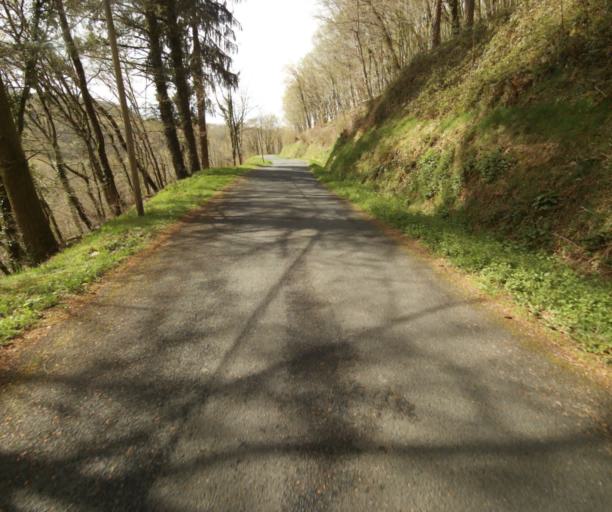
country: FR
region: Limousin
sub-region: Departement de la Correze
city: Laguenne
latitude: 45.2489
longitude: 1.8144
